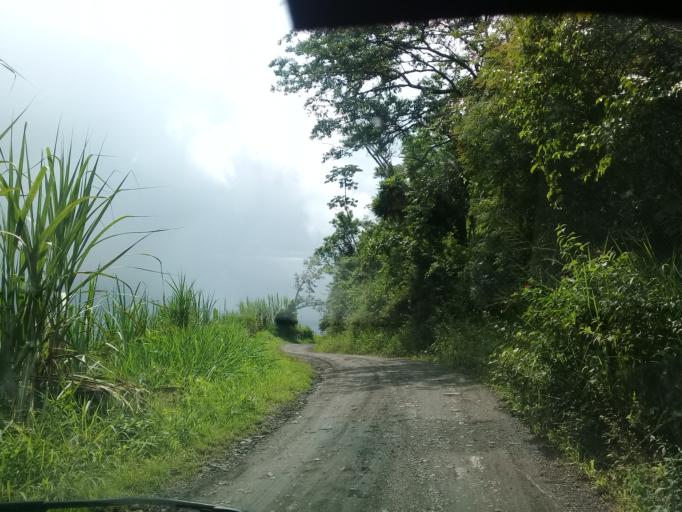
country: CO
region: Cundinamarca
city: Quipile
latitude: 4.7252
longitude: -74.5382
